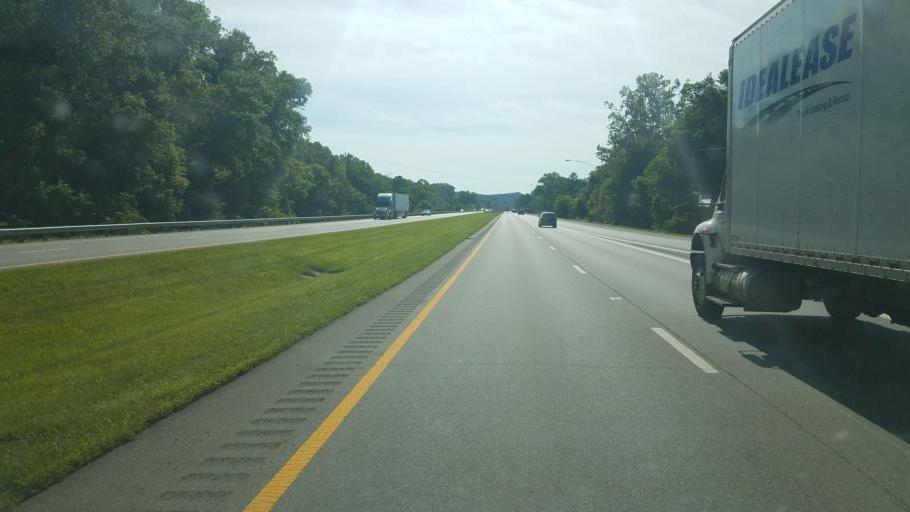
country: US
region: Ohio
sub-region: Hocking County
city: Logan
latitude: 39.5353
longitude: -82.4113
